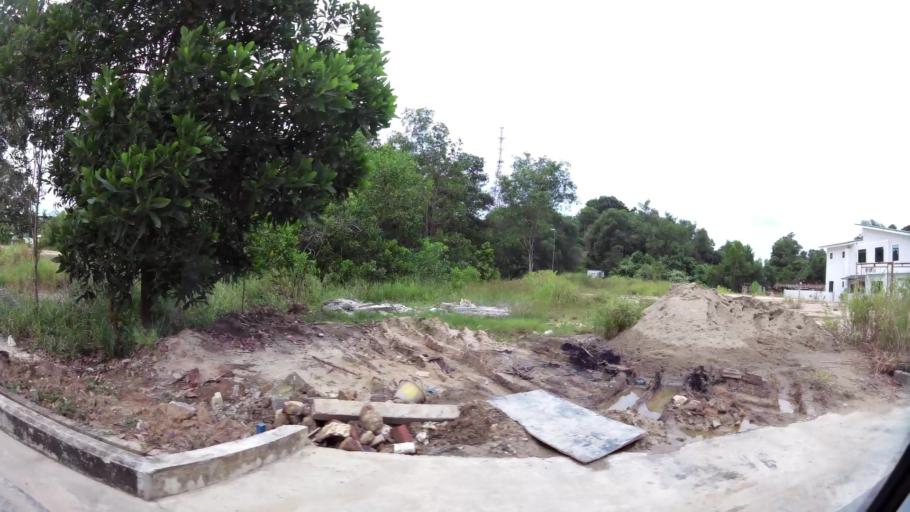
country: BN
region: Brunei and Muara
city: Bandar Seri Begawan
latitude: 4.8866
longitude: 114.9103
